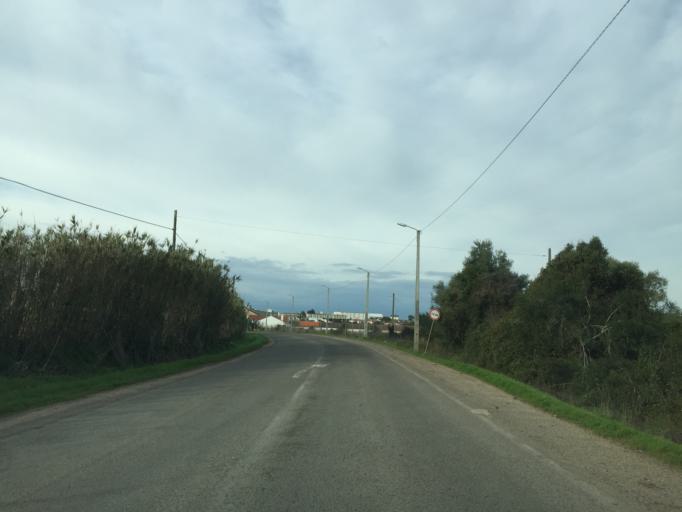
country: PT
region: Lisbon
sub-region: Sintra
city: Almargem
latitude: 38.8699
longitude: -9.2924
